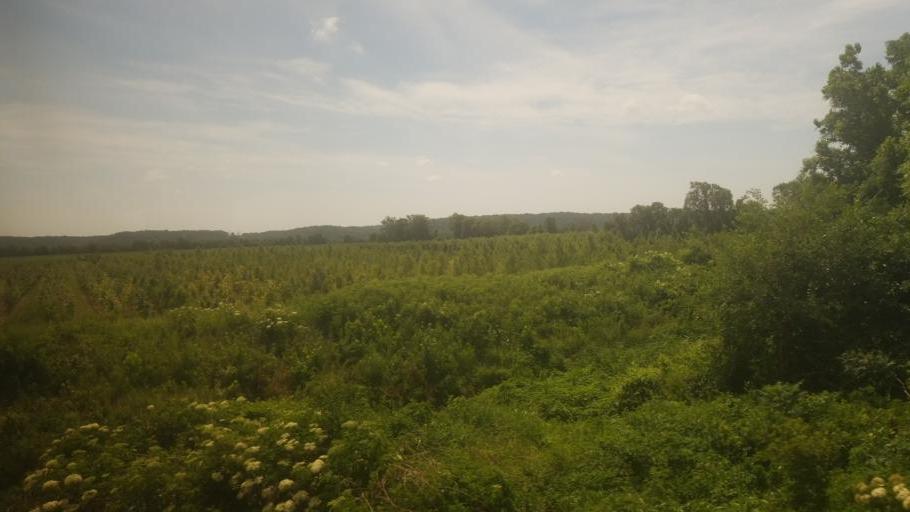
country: US
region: Missouri
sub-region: Jackson County
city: East Independence
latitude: 39.1760
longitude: -94.3298
